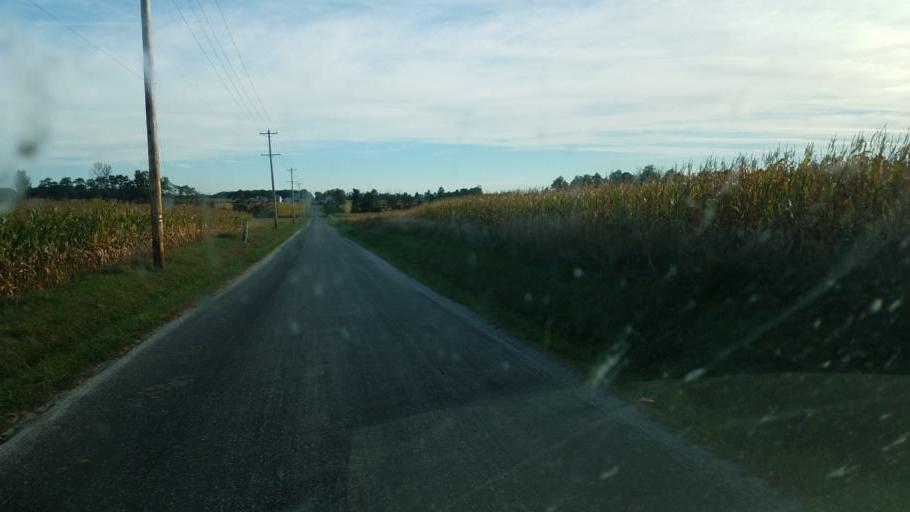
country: US
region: Ohio
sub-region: Ashland County
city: Ashland
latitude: 40.8843
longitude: -82.3878
